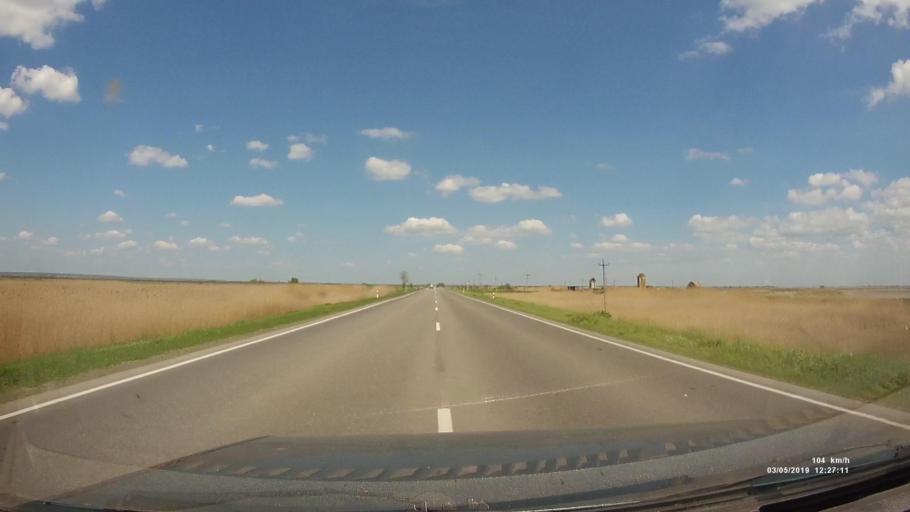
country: RU
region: Rostov
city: Semikarakorsk
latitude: 47.4561
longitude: 40.7193
